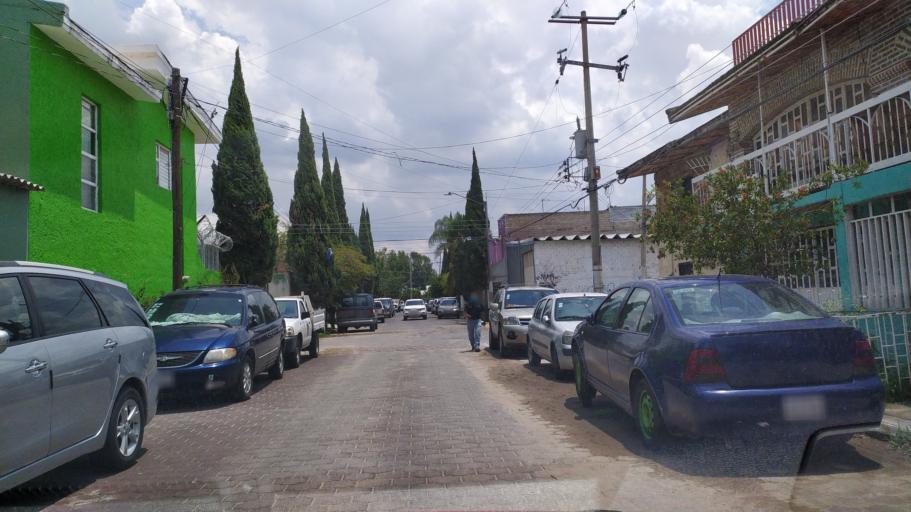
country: MX
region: Jalisco
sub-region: Tlajomulco de Zuniga
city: Palomar
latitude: 20.6392
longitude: -103.4512
